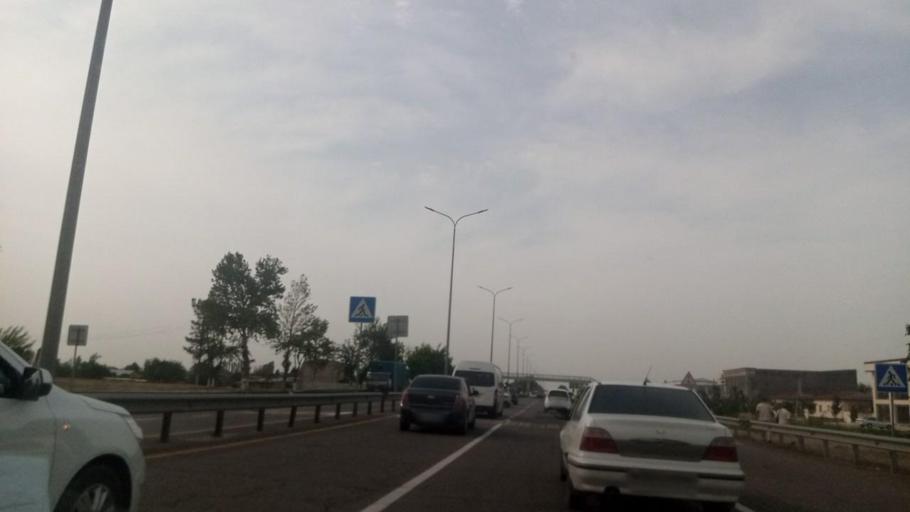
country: UZ
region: Toshkent
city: Tuytepa
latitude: 41.1282
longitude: 69.4375
